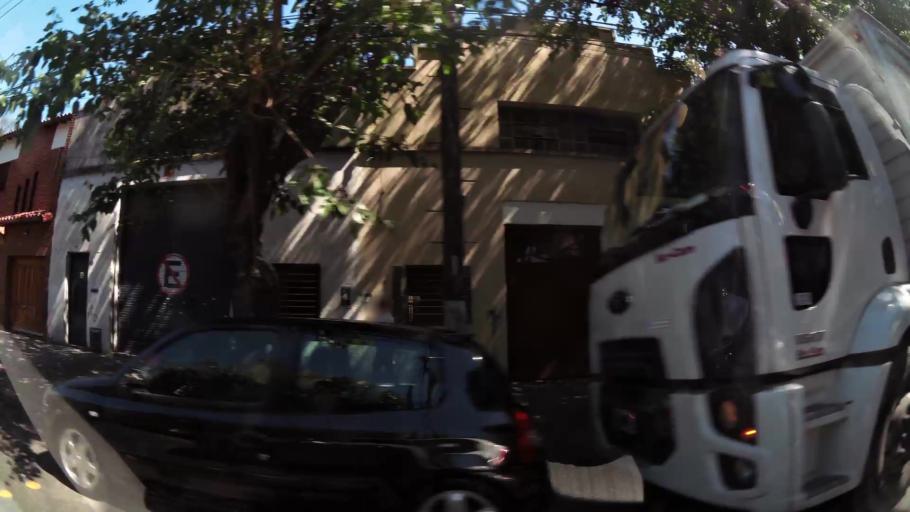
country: AR
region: Buenos Aires
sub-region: Partido de Vicente Lopez
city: Olivos
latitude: -34.5272
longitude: -58.4829
